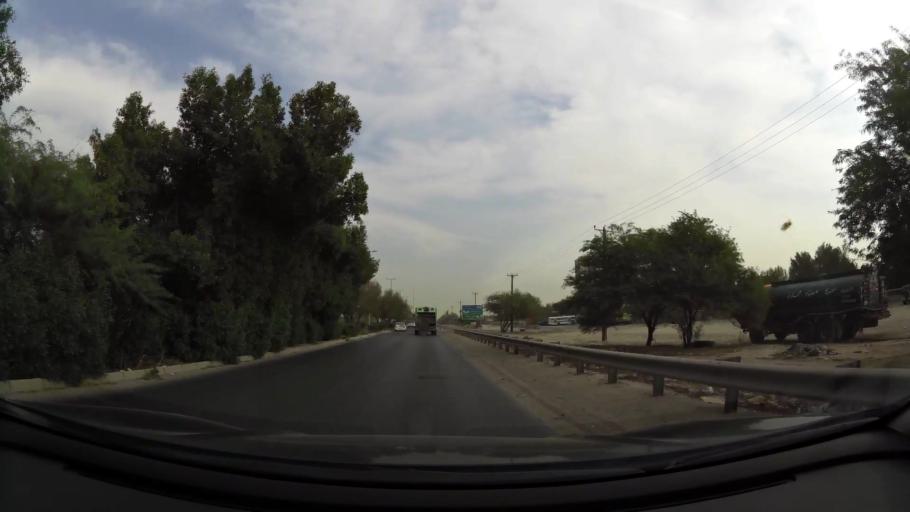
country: KW
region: Muhafazat al Jahra'
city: Al Jahra'
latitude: 29.3185
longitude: 47.7481
